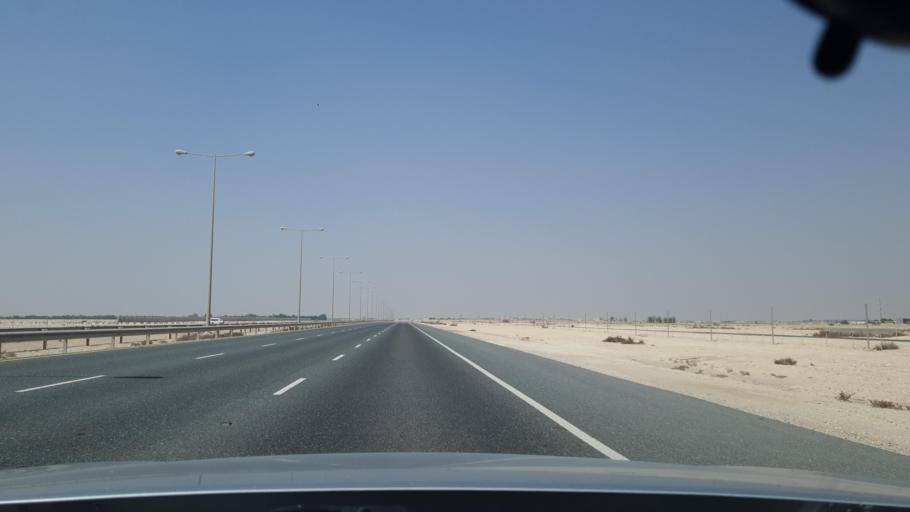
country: QA
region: Al Khawr
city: Al Khawr
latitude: 25.7668
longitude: 51.4179
